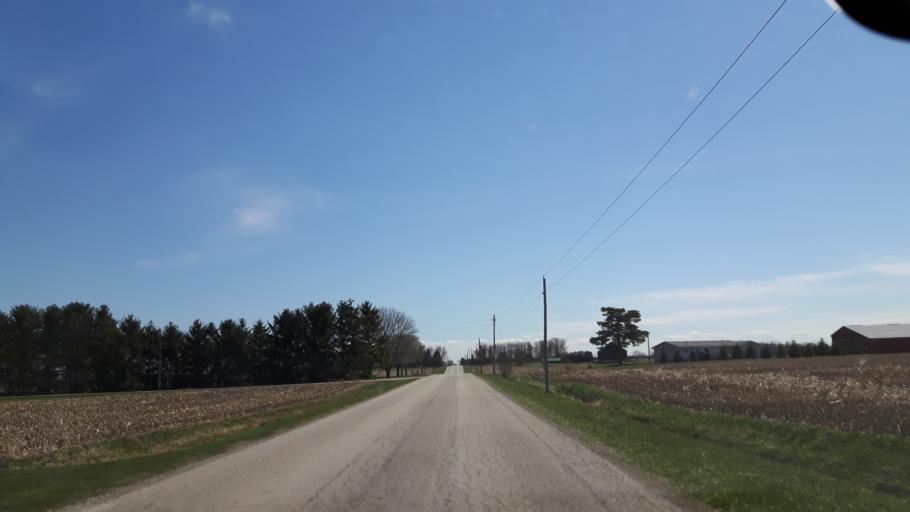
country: CA
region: Ontario
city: Goderich
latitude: 43.6306
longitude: -81.6440
